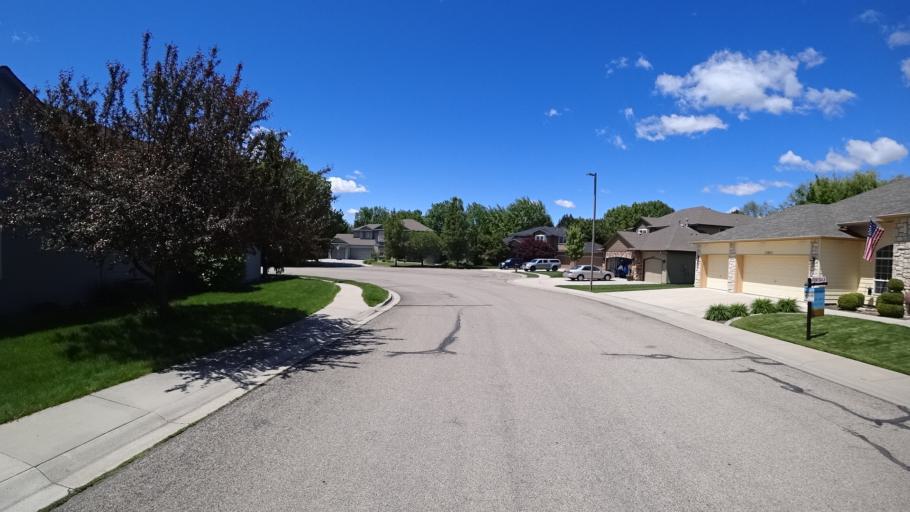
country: US
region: Idaho
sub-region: Ada County
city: Eagle
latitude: 43.6535
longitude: -116.3444
